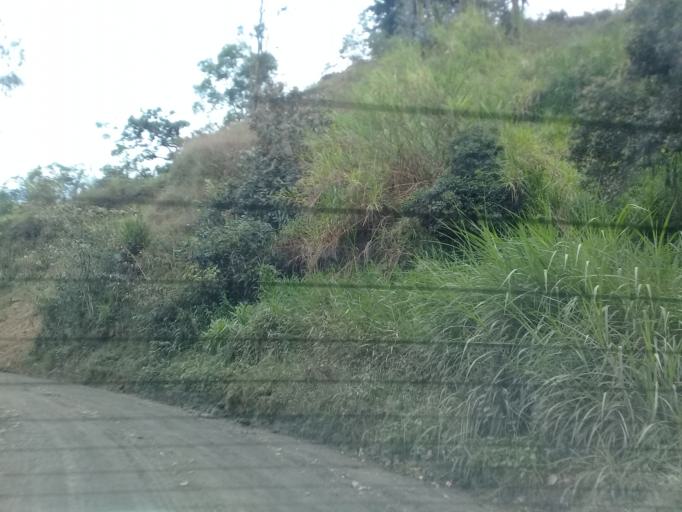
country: CO
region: Cundinamarca
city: Une
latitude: 4.3993
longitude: -73.9883
